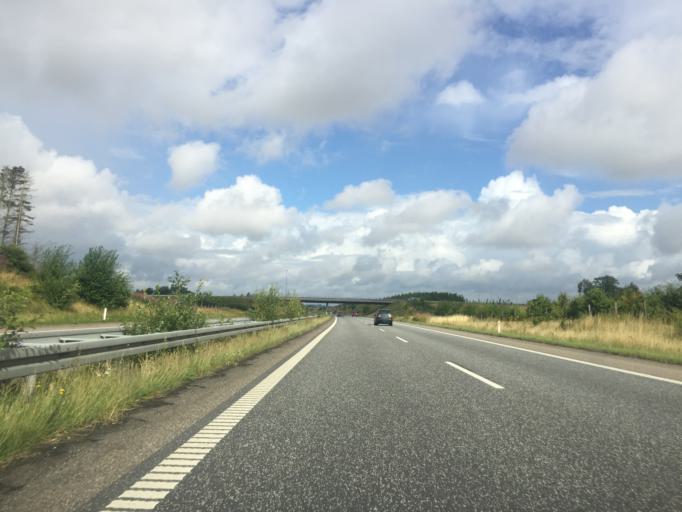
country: DK
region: South Denmark
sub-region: Faaborg-Midtfyn Kommune
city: Arslev
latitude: 55.2801
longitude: 10.4559
